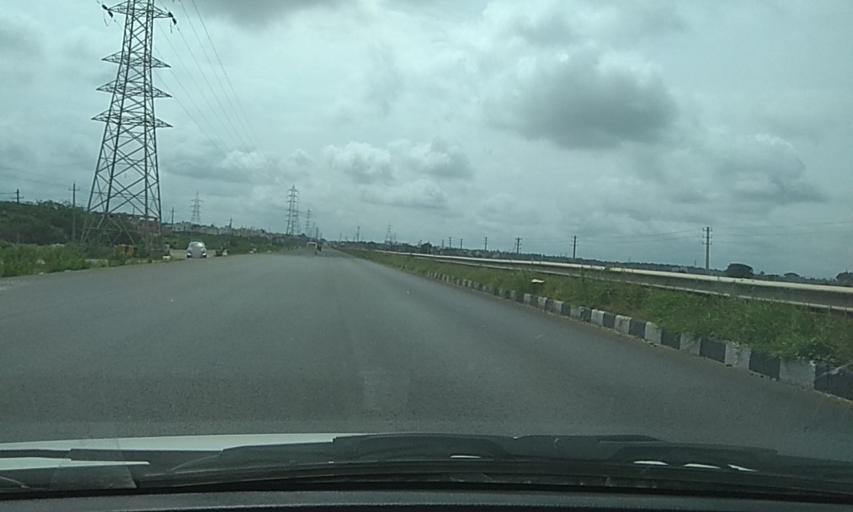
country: IN
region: Karnataka
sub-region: Davanagere
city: Harihar
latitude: 14.4385
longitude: 75.9059
